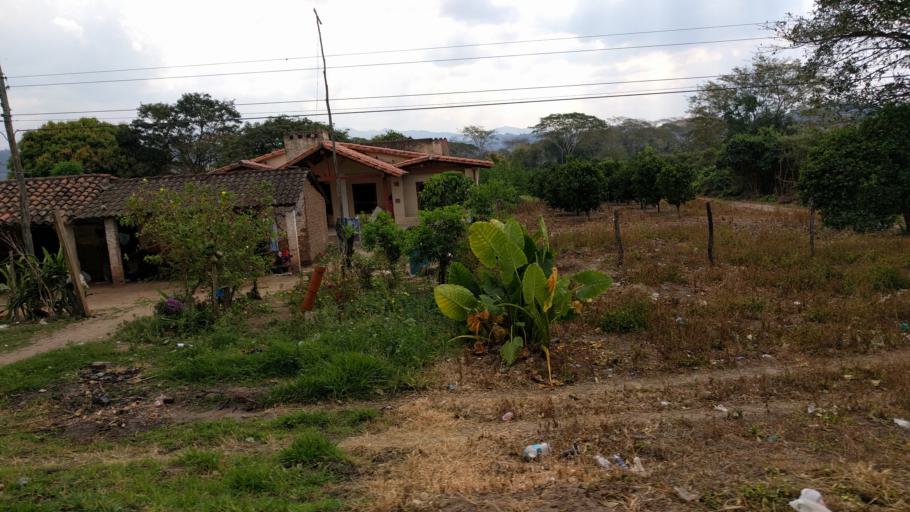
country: BO
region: Santa Cruz
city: Jorochito
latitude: -18.0676
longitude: -63.4381
